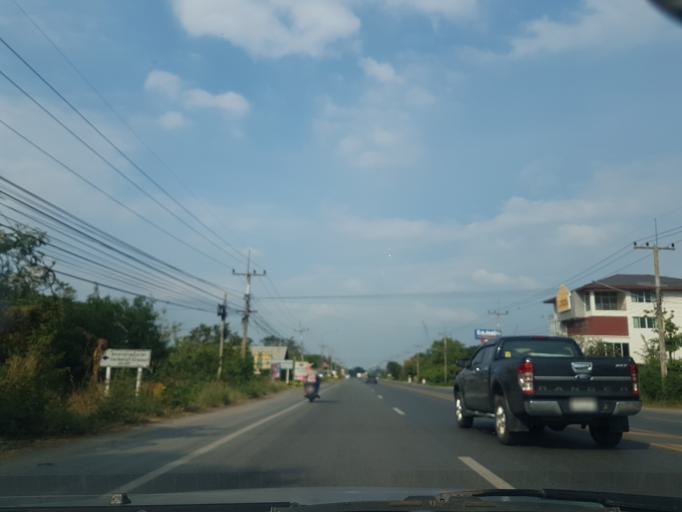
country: TH
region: Sara Buri
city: Ban Mo
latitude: 14.5947
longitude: 100.7330
